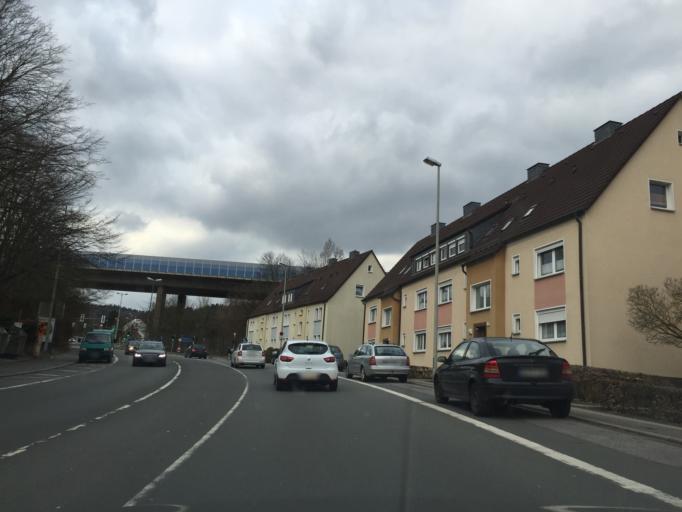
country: DE
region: North Rhine-Westphalia
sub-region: Regierungsbezirk Arnsberg
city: Nachrodt-Wiblingwerde
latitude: 51.3712
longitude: 7.6119
